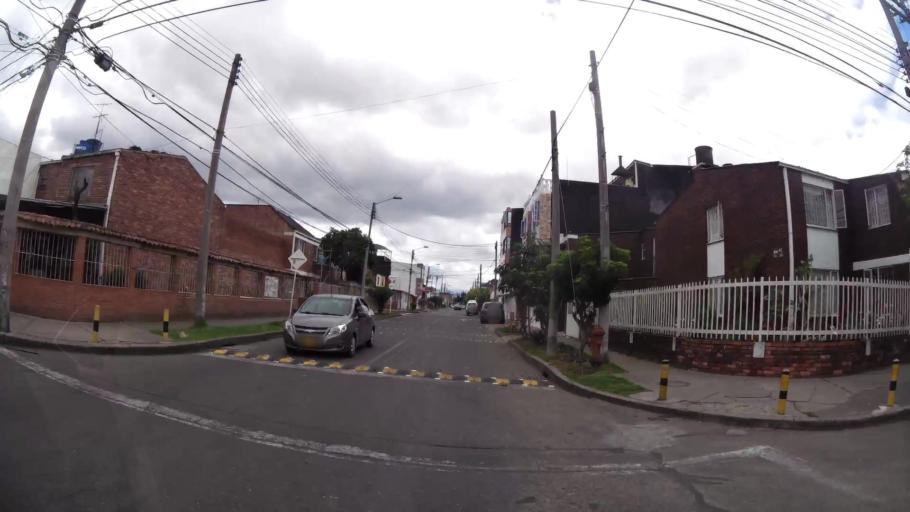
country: CO
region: Bogota D.C.
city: Bogota
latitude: 4.6017
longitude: -74.1172
